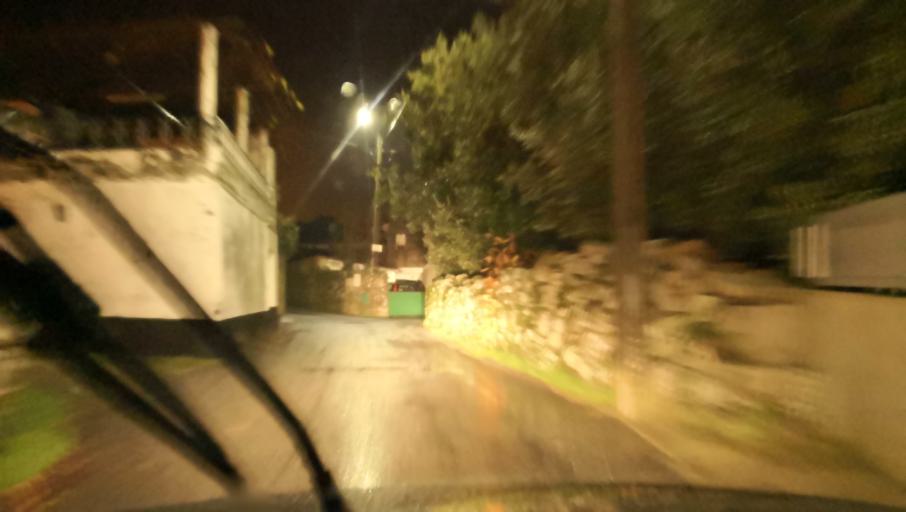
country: PT
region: Vila Real
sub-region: Vila Real
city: Vila Real
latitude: 41.3334
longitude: -7.7238
